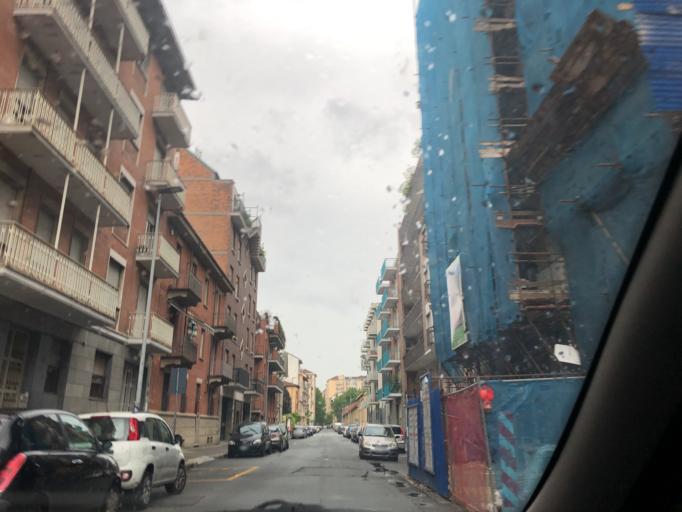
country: IT
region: Piedmont
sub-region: Provincia di Torino
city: Lesna
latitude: 45.0788
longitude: 7.6468
